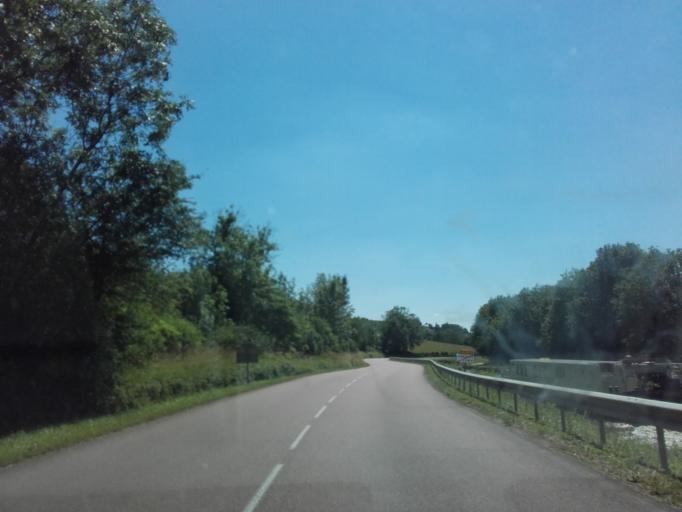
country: FR
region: Bourgogne
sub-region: Departement de Saone-et-Loire
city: Rully
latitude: 46.8963
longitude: 4.6882
